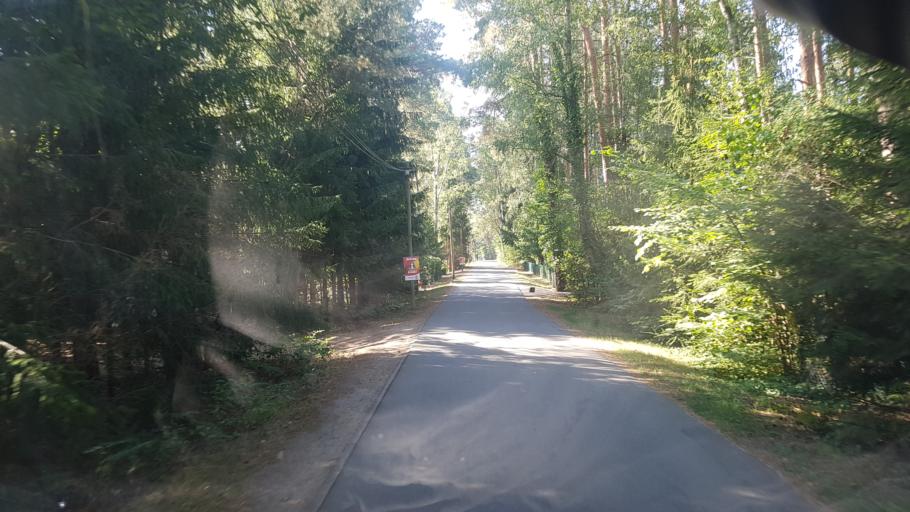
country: DE
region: Brandenburg
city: Plessa
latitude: 51.5157
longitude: 13.6512
